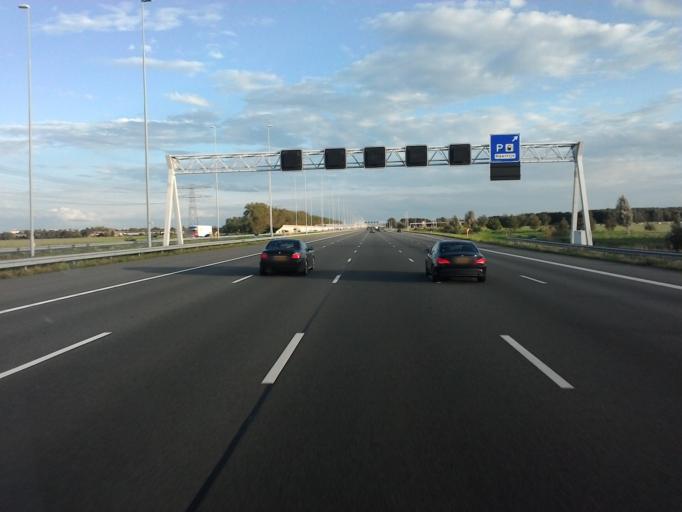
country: NL
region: Utrecht
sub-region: Stichtse Vecht
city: Spechtenkamp
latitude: 52.1500
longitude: 4.9979
